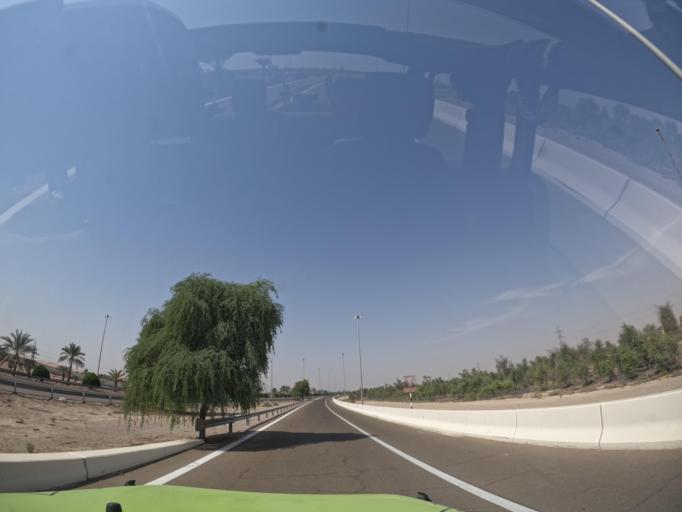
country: AE
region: Abu Dhabi
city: Al Ain
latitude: 24.2040
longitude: 55.3851
